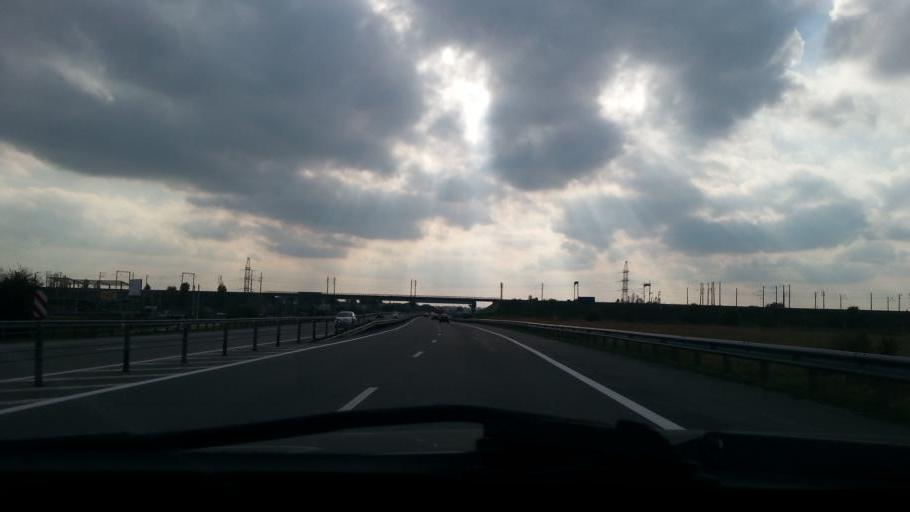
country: RU
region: Rostov
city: Bataysk
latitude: 47.1465
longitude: 39.7026
